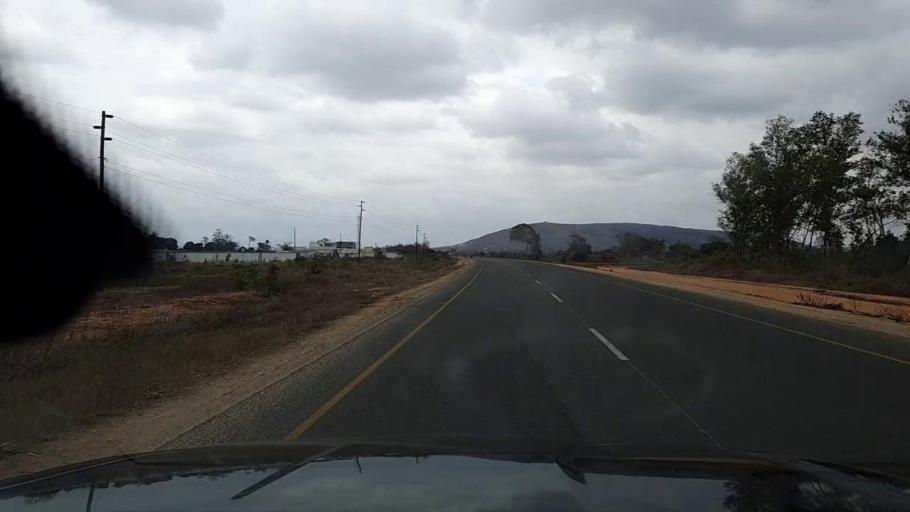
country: MZ
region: Nampula
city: Nampula
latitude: -15.1620
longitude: 39.3068
